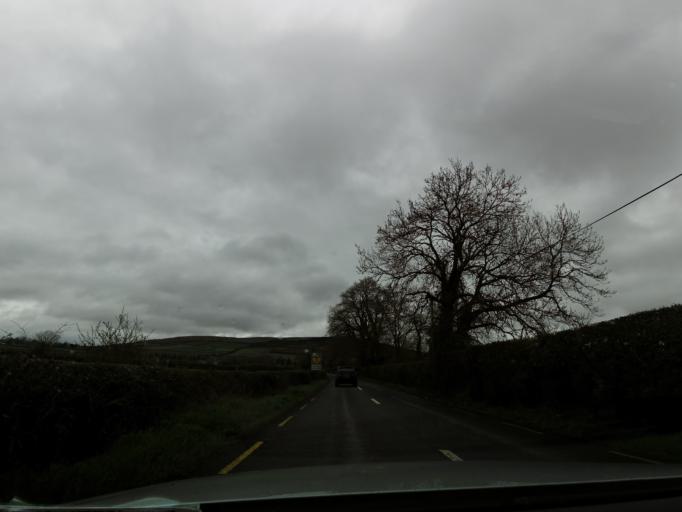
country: IE
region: Leinster
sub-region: Laois
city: Rathdowney
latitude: 52.7223
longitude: -7.5272
